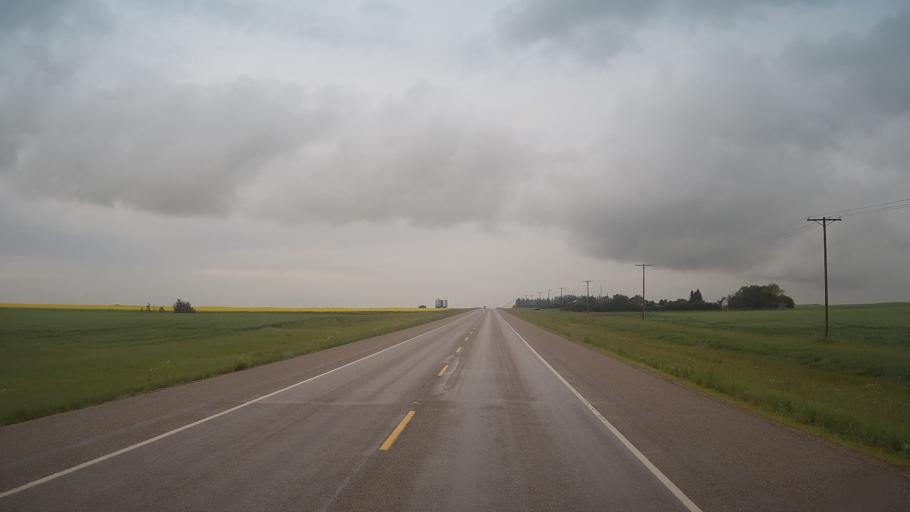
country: CA
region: Saskatchewan
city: Wilkie
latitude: 52.4056
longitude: -108.7810
